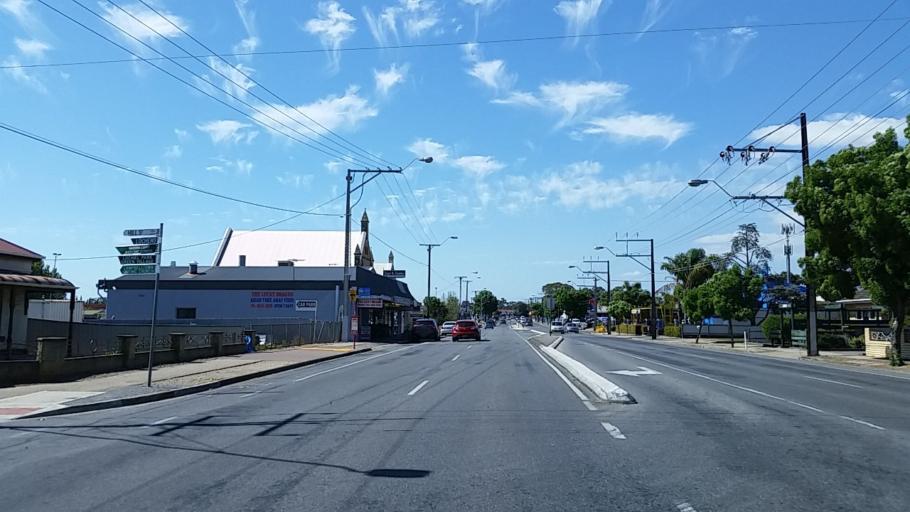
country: AU
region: South Australia
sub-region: Campbelltown
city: Campbelltown
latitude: -34.8803
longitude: 138.6622
